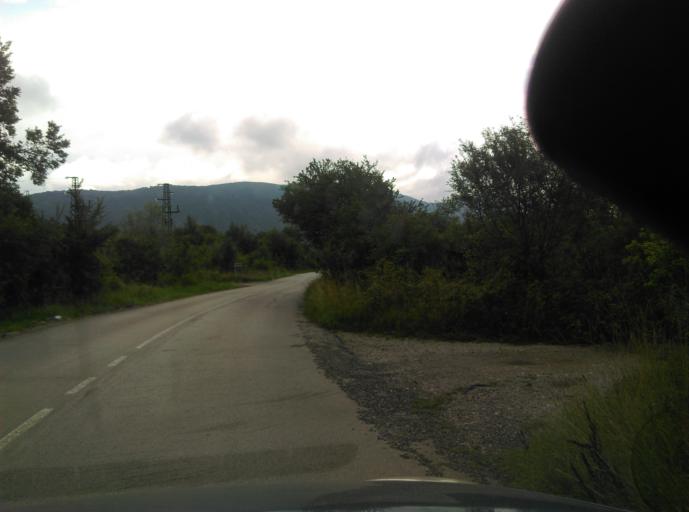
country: BG
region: Sofia-Capital
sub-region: Stolichna Obshtina
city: Sofia
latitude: 42.5893
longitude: 23.4008
